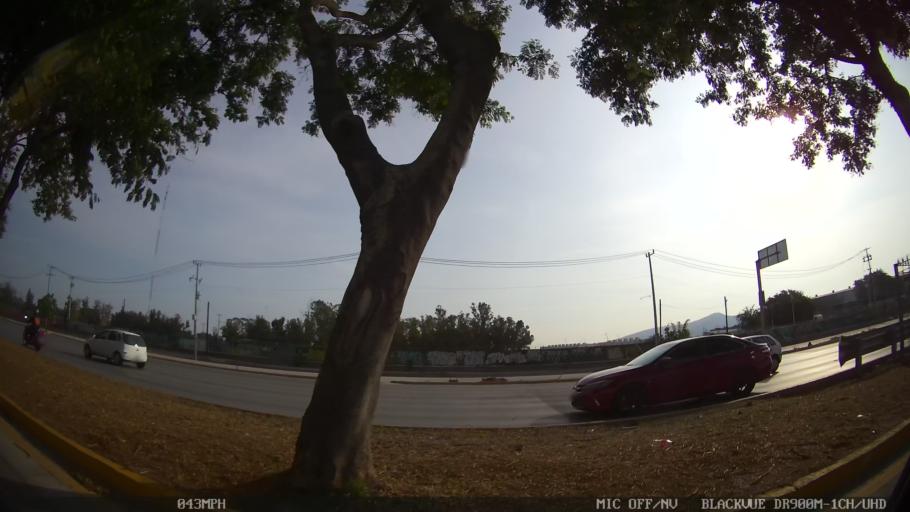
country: MX
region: Jalisco
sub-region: Zapopan
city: Zapopan
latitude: 20.7175
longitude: -103.3099
